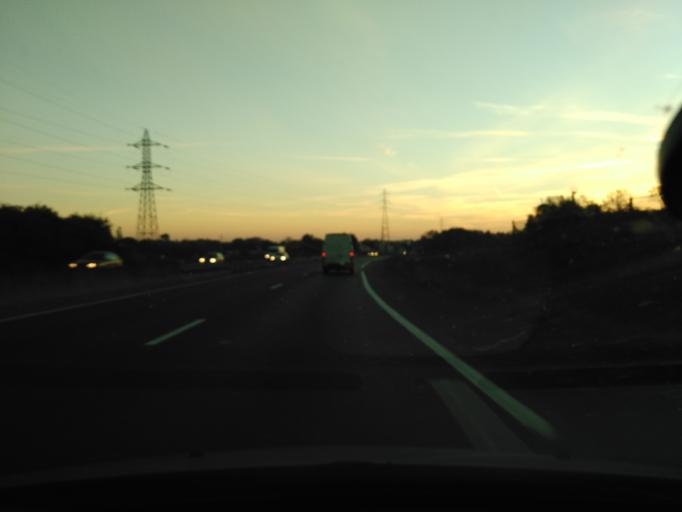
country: FR
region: Poitou-Charentes
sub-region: Departement de la Charente-Maritime
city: Lagord
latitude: 46.1811
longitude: -1.1464
